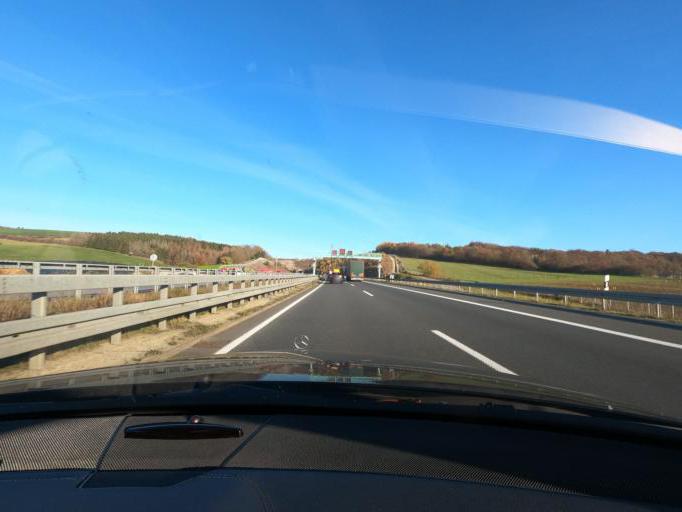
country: DE
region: Thuringia
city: Arenshausen
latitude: 51.3990
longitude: 9.9749
